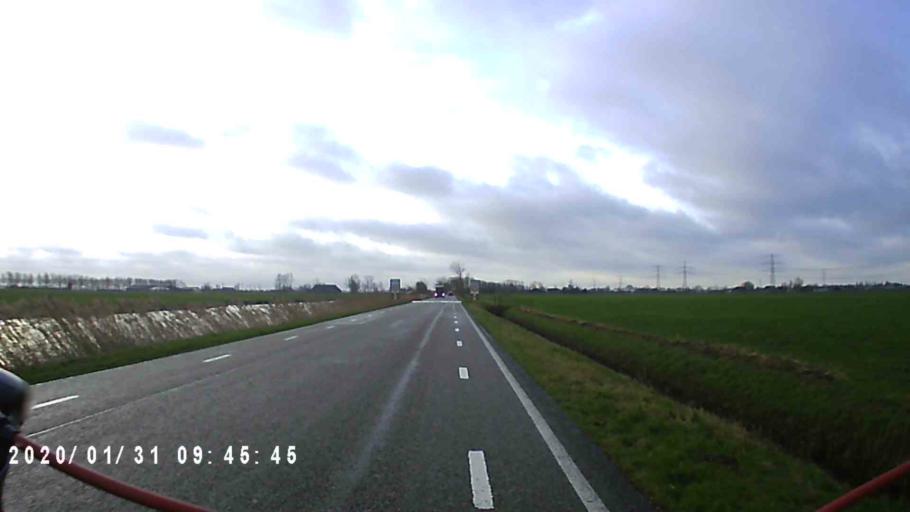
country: NL
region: Groningen
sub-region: Gemeente Zuidhorn
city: Aduard
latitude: 53.2682
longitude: 6.4834
